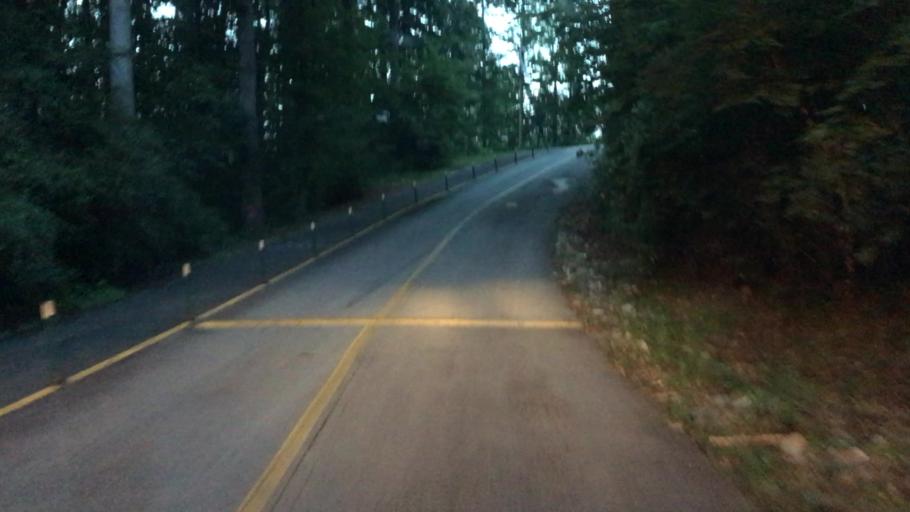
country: US
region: Georgia
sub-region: Jackson County
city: Braselton
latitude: 34.1464
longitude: -83.8170
